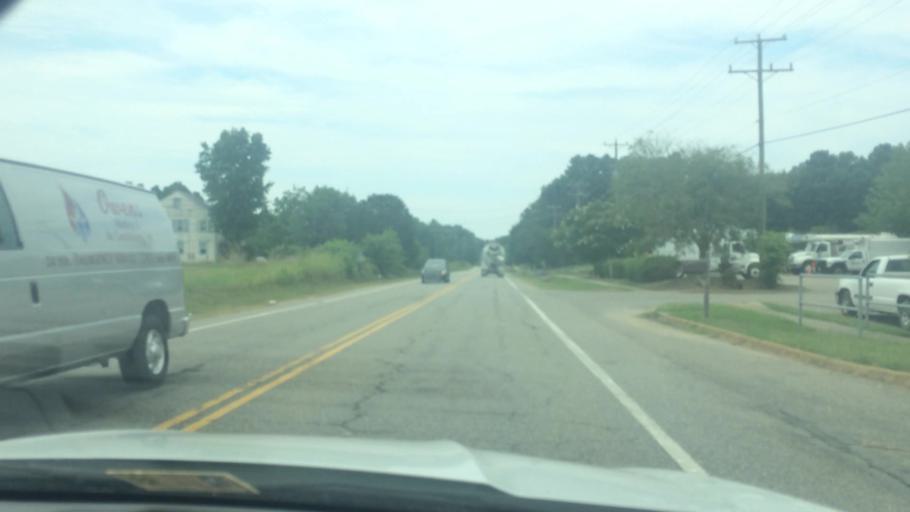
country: US
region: Virginia
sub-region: James City County
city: Williamsburg
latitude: 37.2799
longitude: -76.8054
